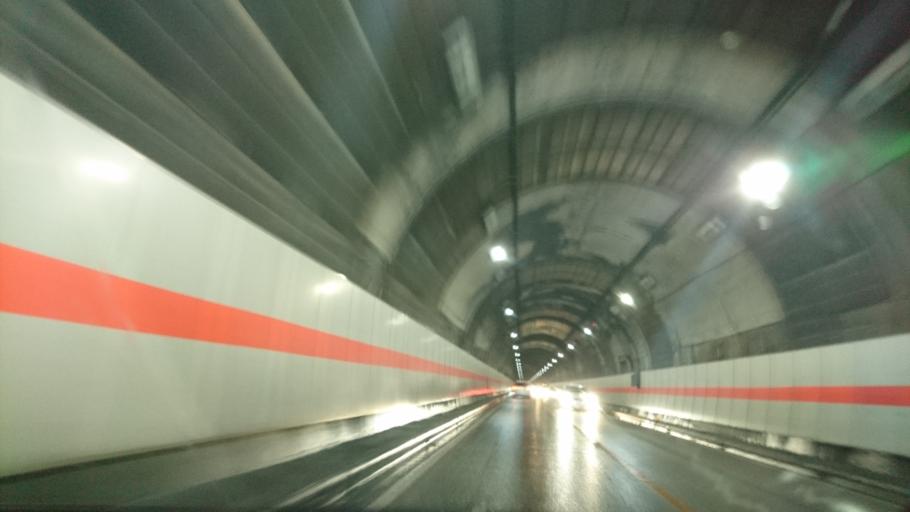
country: JP
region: Miyagi
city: Ishinomaki
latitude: 38.4339
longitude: 141.3208
